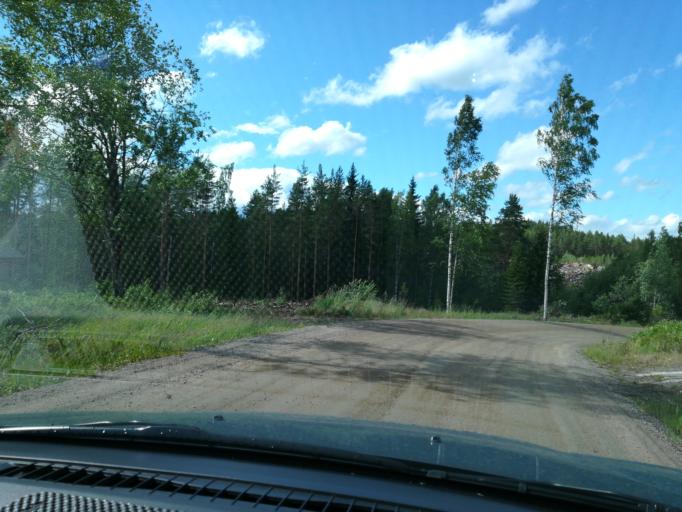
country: FI
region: South Karelia
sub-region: Lappeenranta
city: Savitaipale
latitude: 61.3004
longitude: 27.6399
